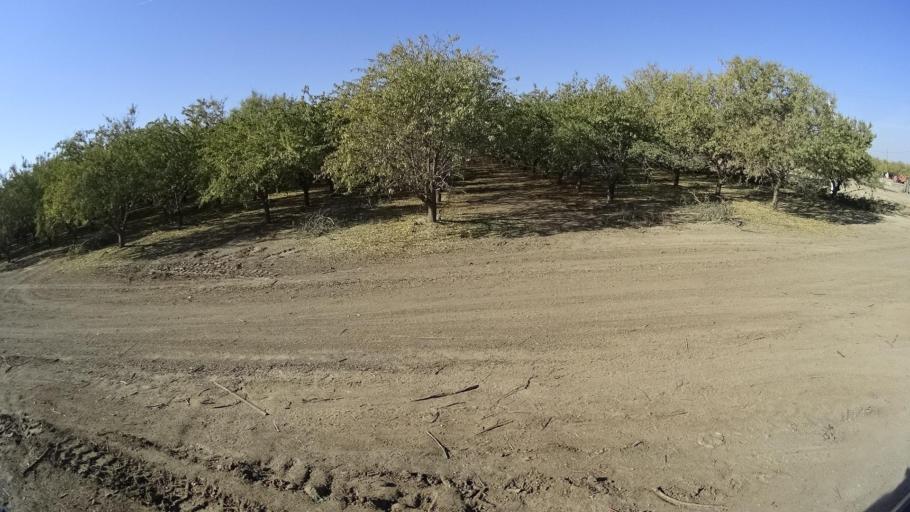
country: US
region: California
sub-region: Kern County
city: Wasco
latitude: 35.7318
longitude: -119.4193
